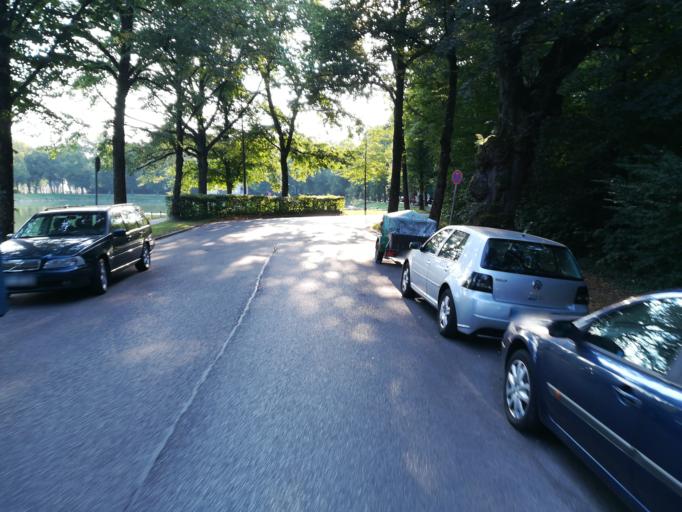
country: DE
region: Bavaria
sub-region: Upper Bavaria
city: Munich
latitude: 48.1589
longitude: 11.5273
